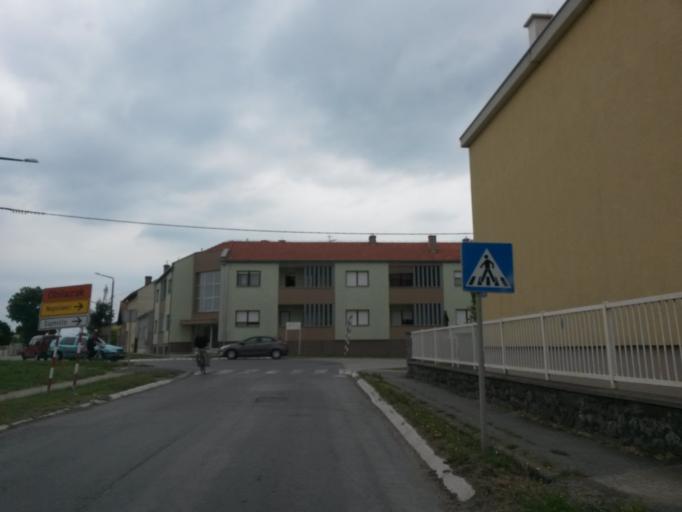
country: HR
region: Vukovarsko-Srijemska
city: Vukovar
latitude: 45.3442
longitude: 18.9978
